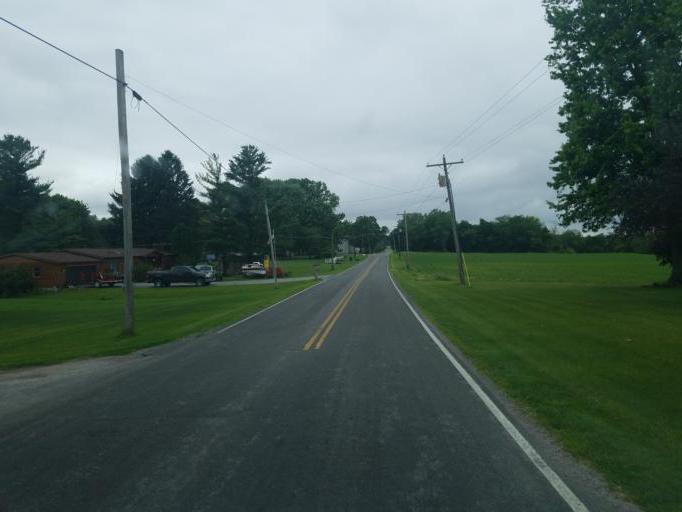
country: US
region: Ohio
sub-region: Marion County
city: Marion
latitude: 40.5130
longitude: -83.0475
